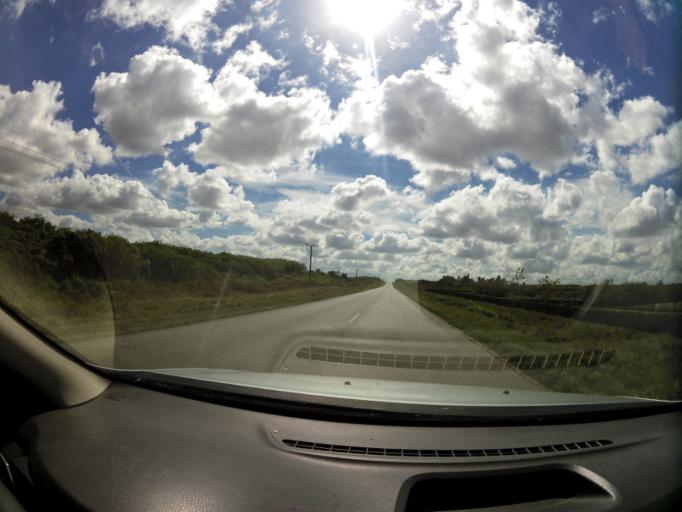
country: CU
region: Las Tunas
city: Las Tunas
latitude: 20.8836
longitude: -76.9125
